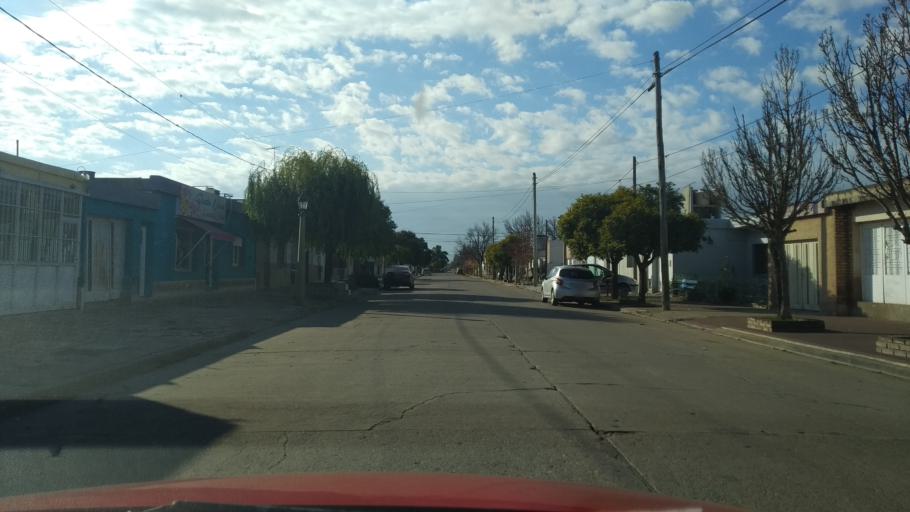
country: AR
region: Cordoba
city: Leones
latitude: -32.6583
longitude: -62.3006
